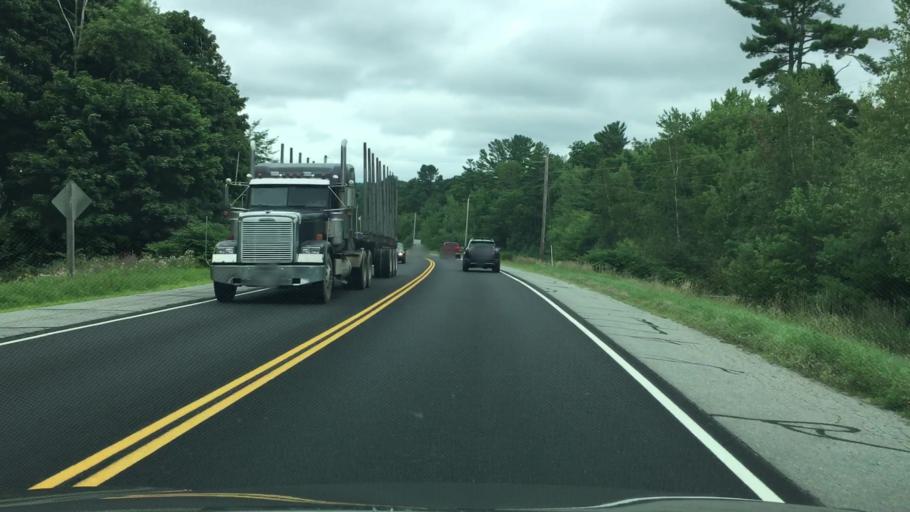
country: US
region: Maine
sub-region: Penobscot County
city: Orrington
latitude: 44.6905
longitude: -68.8108
